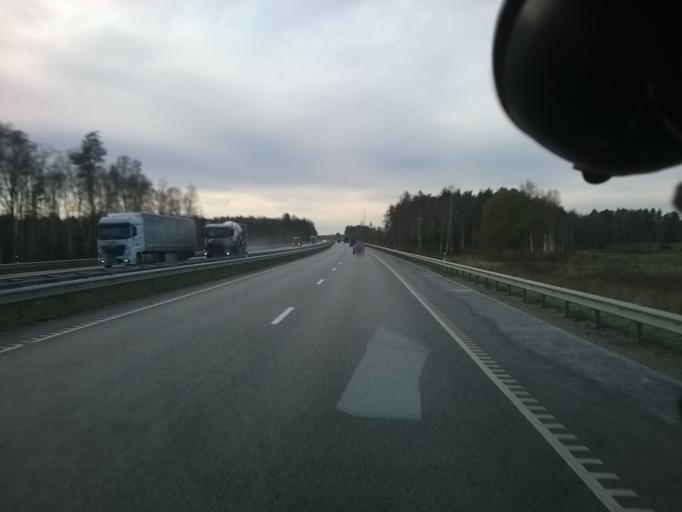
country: EE
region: Harju
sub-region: Kiili vald
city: Kiili
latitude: 59.3325
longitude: 24.7982
